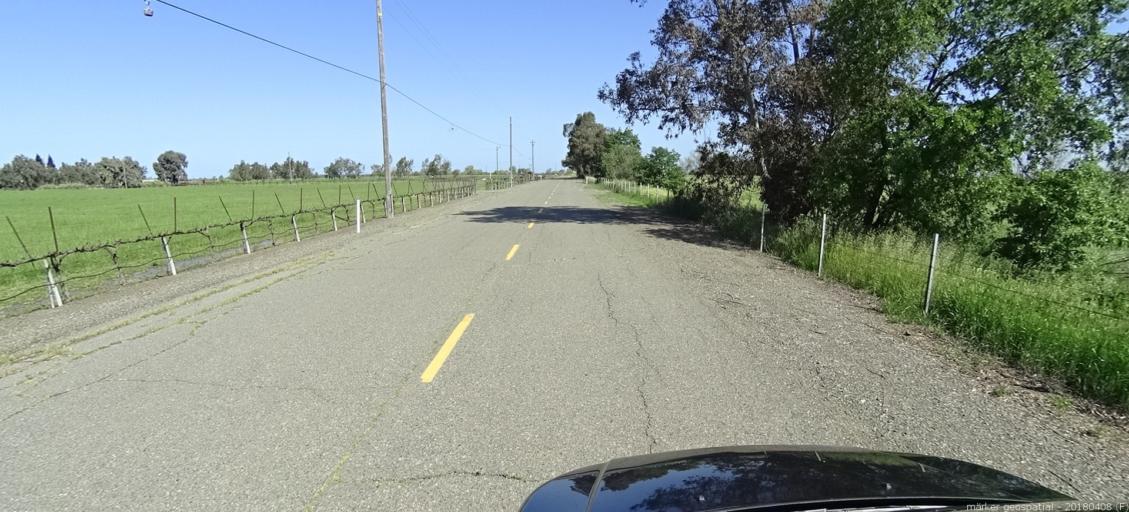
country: US
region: California
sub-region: Sacramento County
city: Laguna
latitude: 38.3339
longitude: -121.4688
